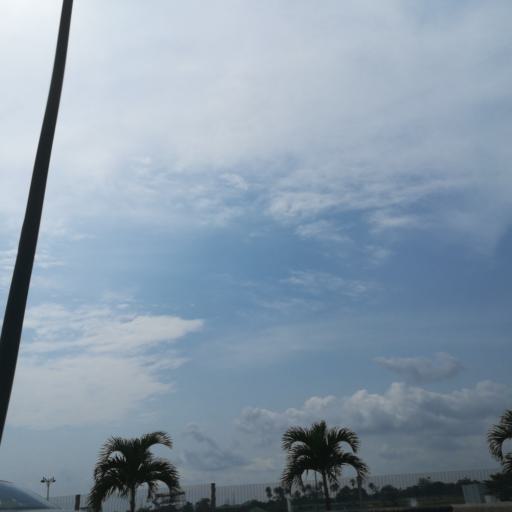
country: NG
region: Rivers
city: Port Harcourt
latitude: 4.8375
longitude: 7.0143
